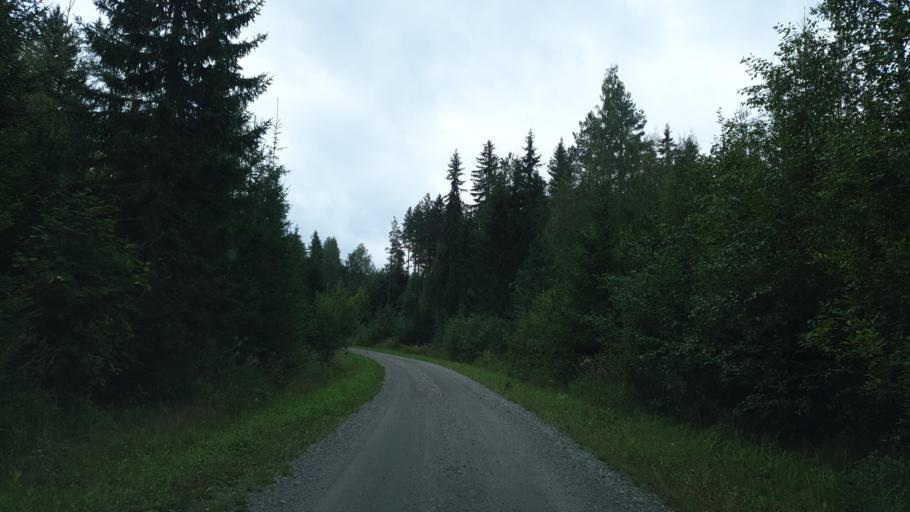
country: FI
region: Northern Savo
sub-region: Kuopio
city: Nilsiae
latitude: 63.2437
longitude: 28.2552
